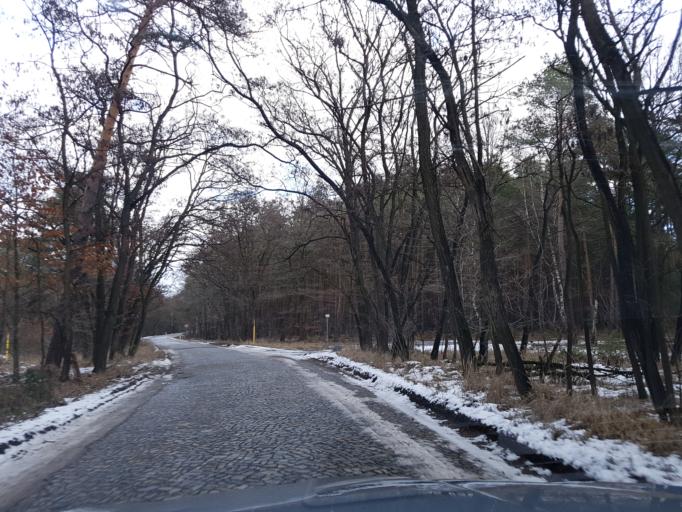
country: DE
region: Brandenburg
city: Merzdorf
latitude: 51.3909
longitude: 13.5227
